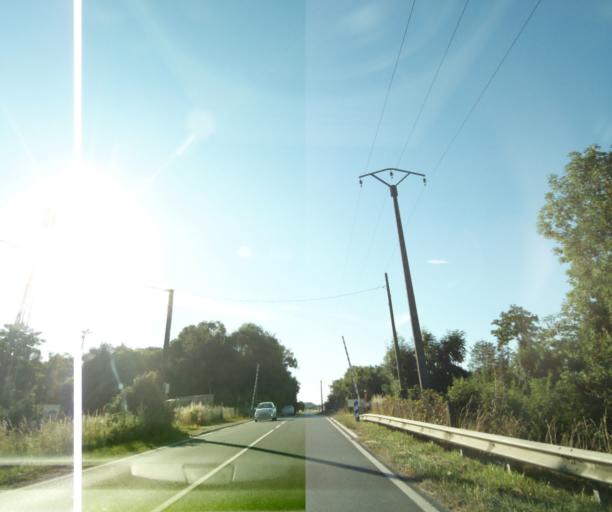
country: FR
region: Ile-de-France
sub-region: Departement de Seine-et-Marne
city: Cannes-Ecluse
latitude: 48.3812
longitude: 2.9770
